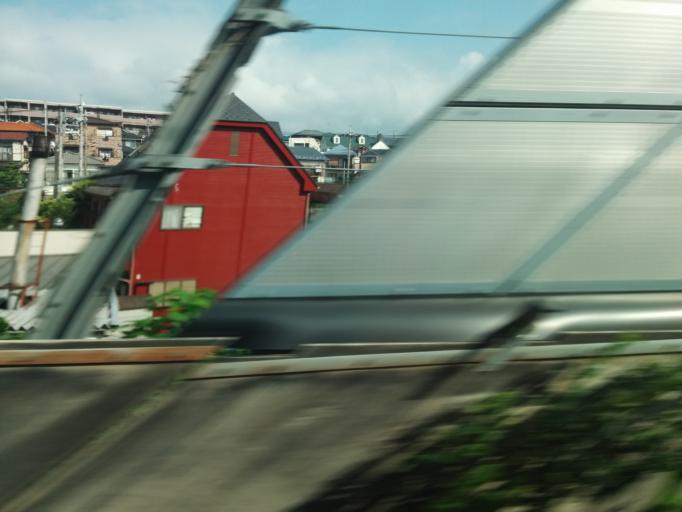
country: JP
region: Kanagawa
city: Minami-rinkan
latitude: 35.4513
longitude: 139.5194
